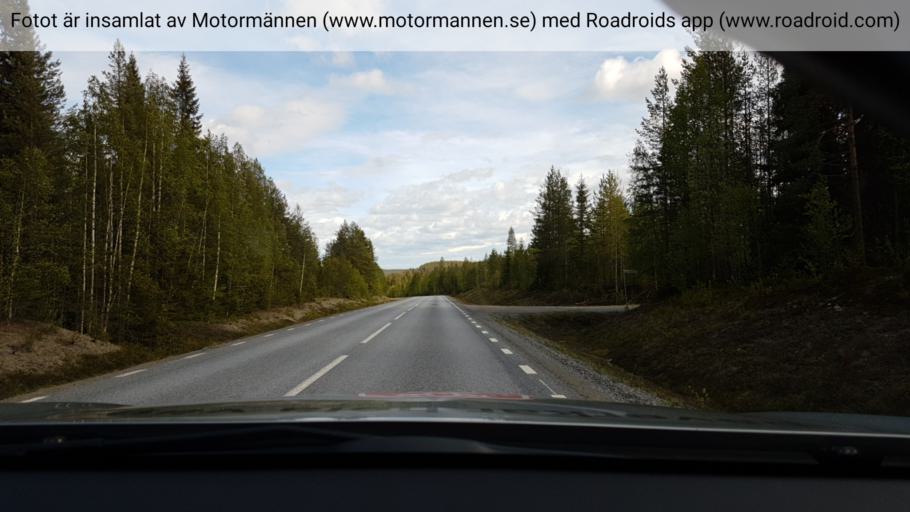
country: SE
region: Vaesterbotten
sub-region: Lycksele Kommun
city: Lycksele
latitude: 64.0294
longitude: 18.6332
